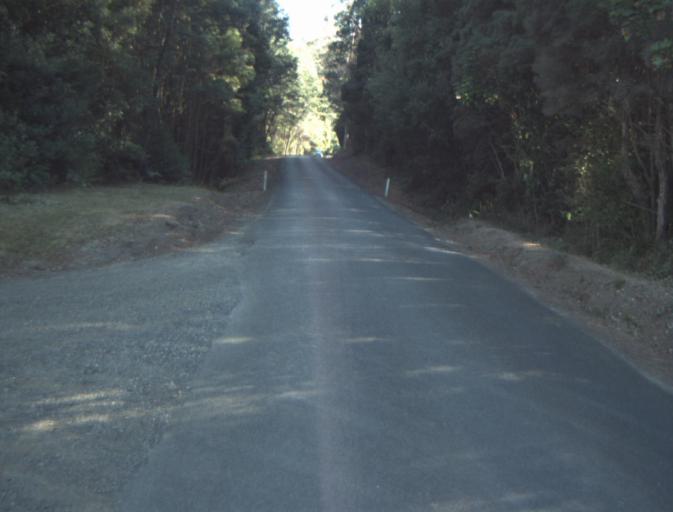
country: AU
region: Tasmania
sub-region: Launceston
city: Mayfield
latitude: -41.3034
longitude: 147.1985
